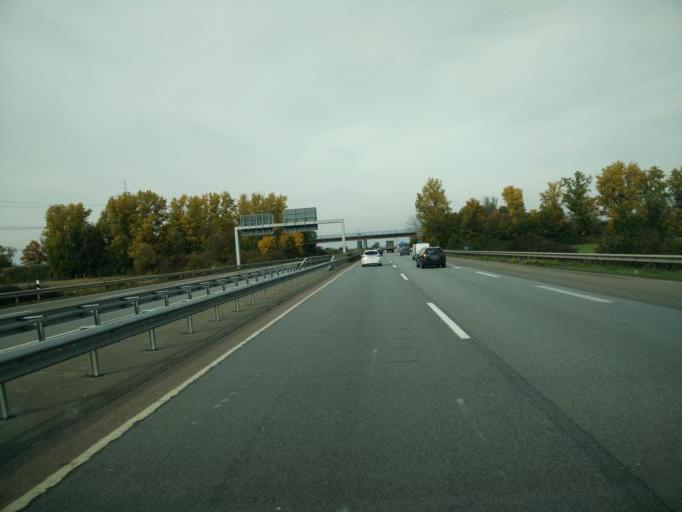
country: DE
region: Rheinland-Pfalz
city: Dannstadt-Schauernheim
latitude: 49.4464
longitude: 8.3215
